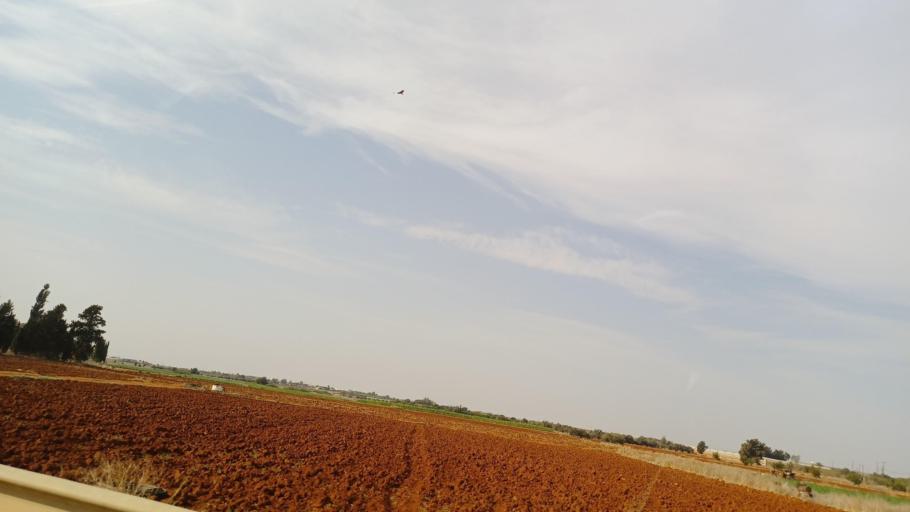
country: CY
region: Ammochostos
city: Liopetri
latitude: 35.0230
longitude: 33.9058
